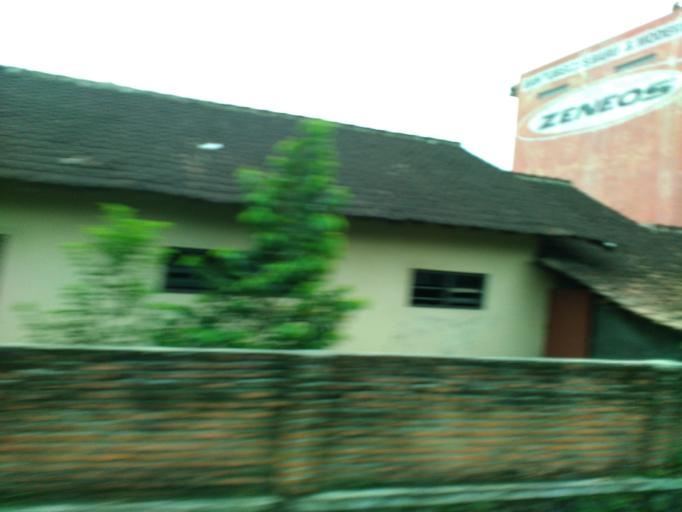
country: ID
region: Central Java
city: Gatak
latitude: -7.5927
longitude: 110.7027
